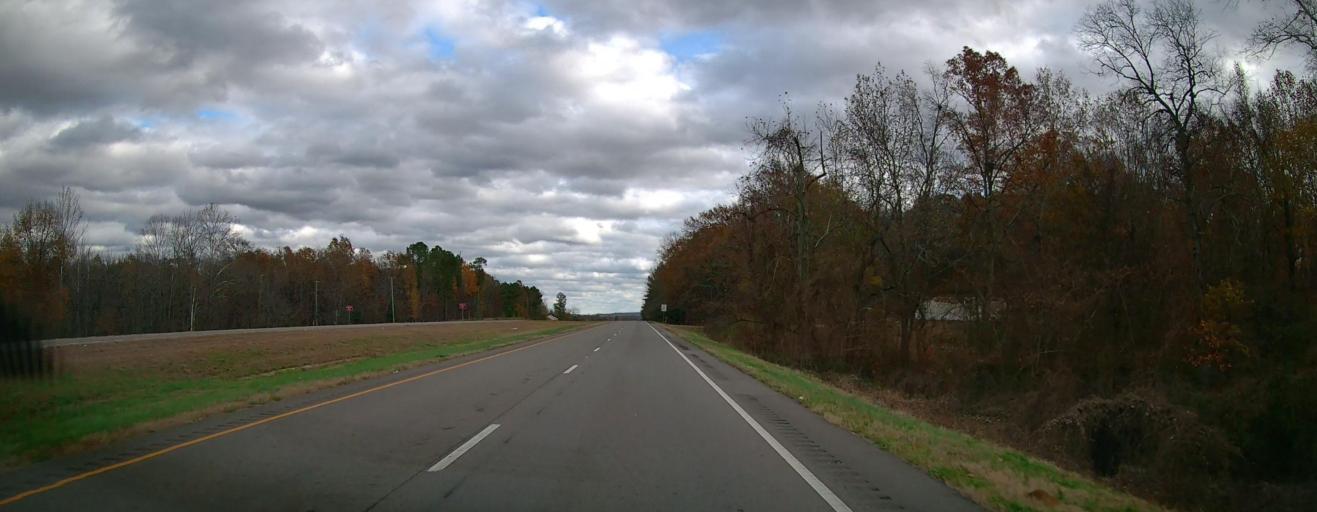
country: US
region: Alabama
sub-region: Morgan County
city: Danville
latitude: 34.3884
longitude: -87.1098
